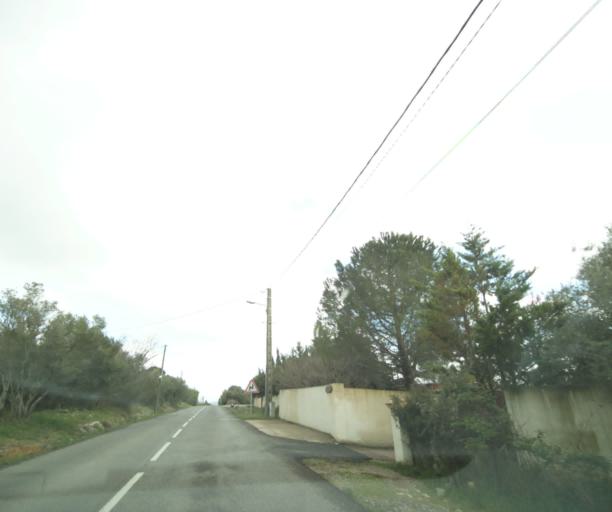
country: FR
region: Languedoc-Roussillon
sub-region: Departement de l'Herault
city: Pignan
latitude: 43.5907
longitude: 3.7519
